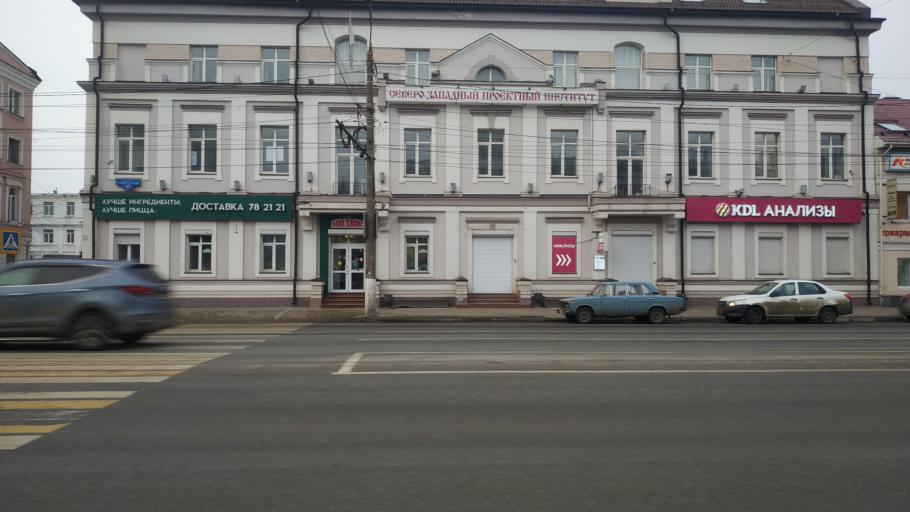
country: RU
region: Tverskaya
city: Tver
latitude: 56.8576
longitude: 35.9256
